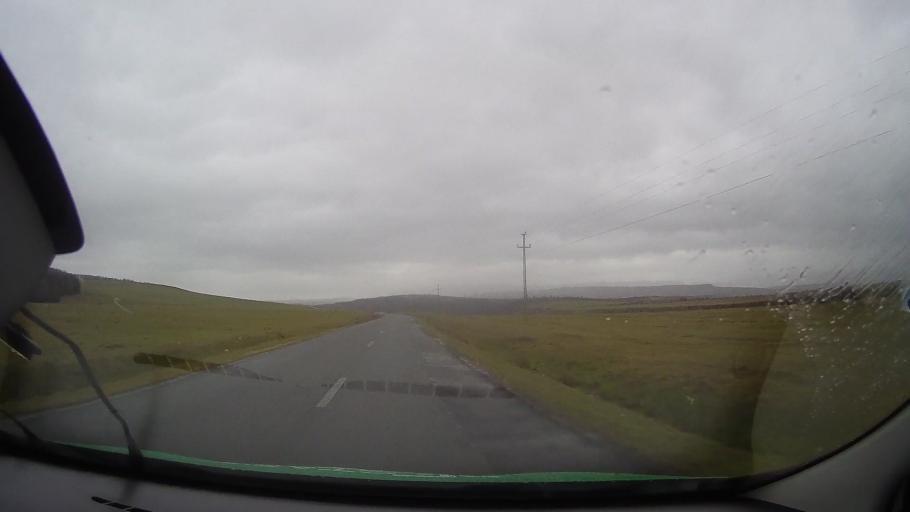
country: RO
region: Mures
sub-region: Comuna Brancovenesti
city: Valenii de Mures
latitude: 46.9058
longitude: 24.7846
